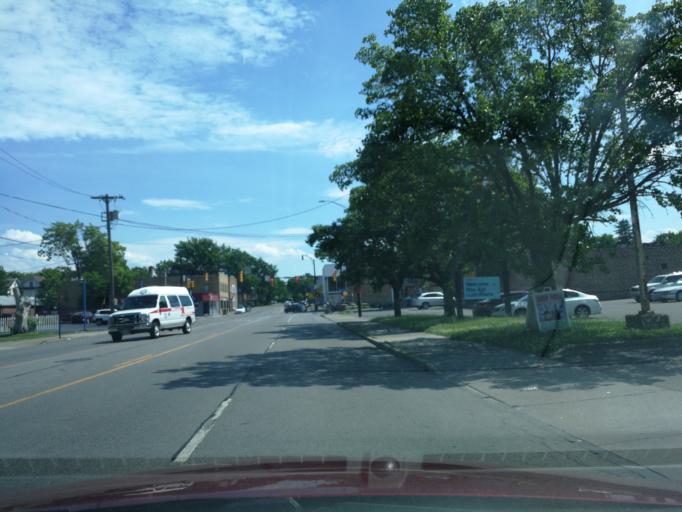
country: US
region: New York
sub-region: Monroe County
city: Irondequoit
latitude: 43.1882
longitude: -77.5842
